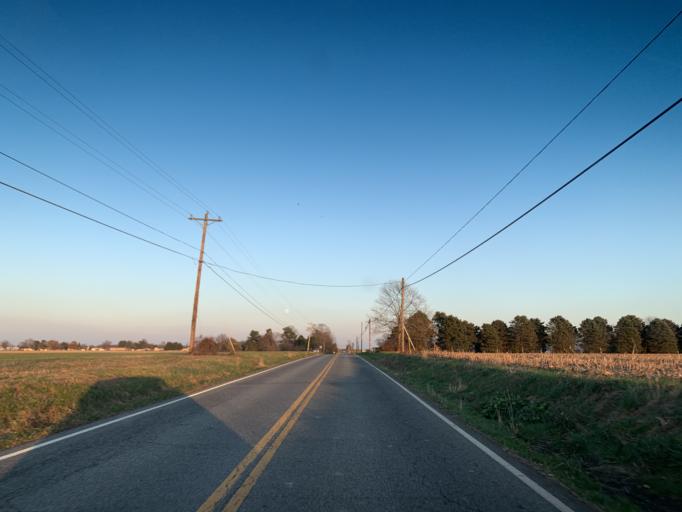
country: US
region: Maryland
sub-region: Cecil County
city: Charlestown
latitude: 39.4091
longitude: -75.9266
